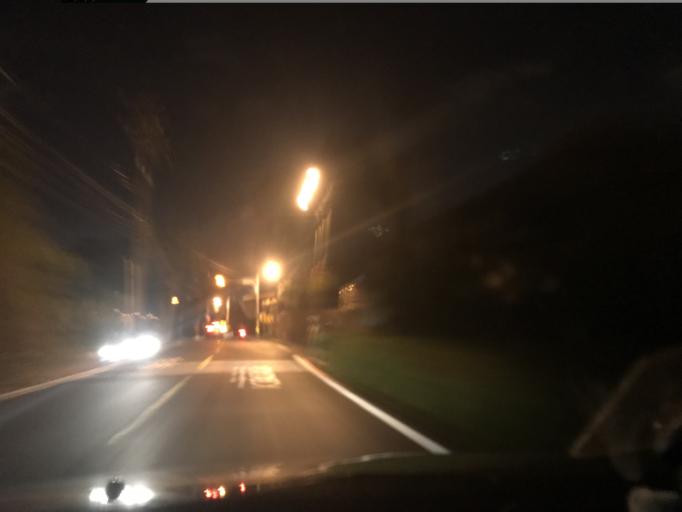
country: TW
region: Taiwan
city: Taoyuan City
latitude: 24.9429
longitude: 121.2359
